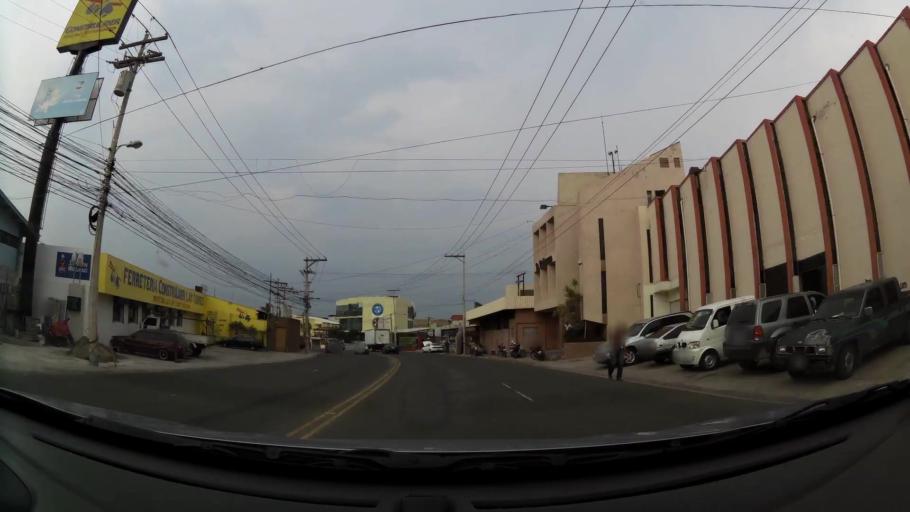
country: HN
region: Francisco Morazan
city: Tegucigalpa
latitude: 14.0604
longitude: -87.2253
